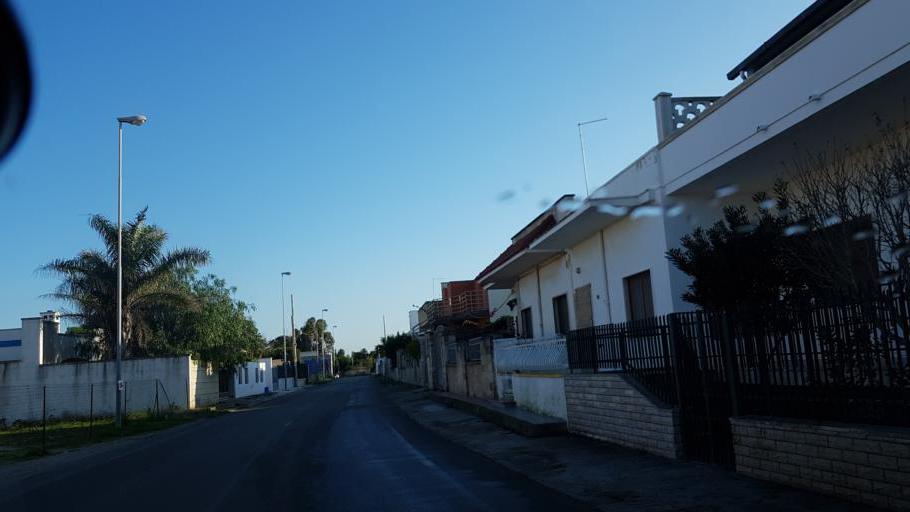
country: IT
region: Apulia
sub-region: Provincia di Brindisi
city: Torchiarolo
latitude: 40.5011
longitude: 18.1154
